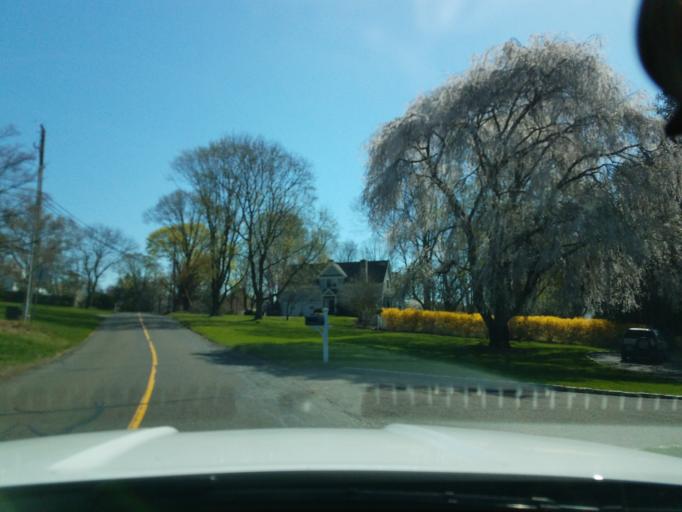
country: US
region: Connecticut
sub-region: Fairfield County
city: Southport
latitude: 41.1309
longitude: -73.3104
